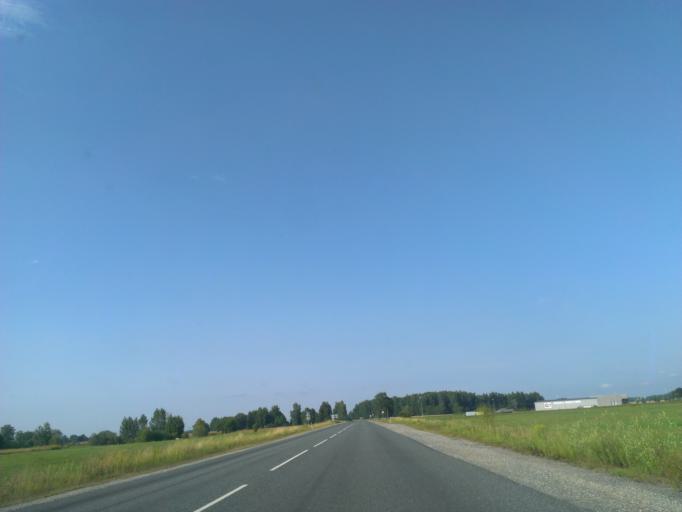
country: LV
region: Priekuli
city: Priekuli
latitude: 57.3132
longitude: 25.3190
